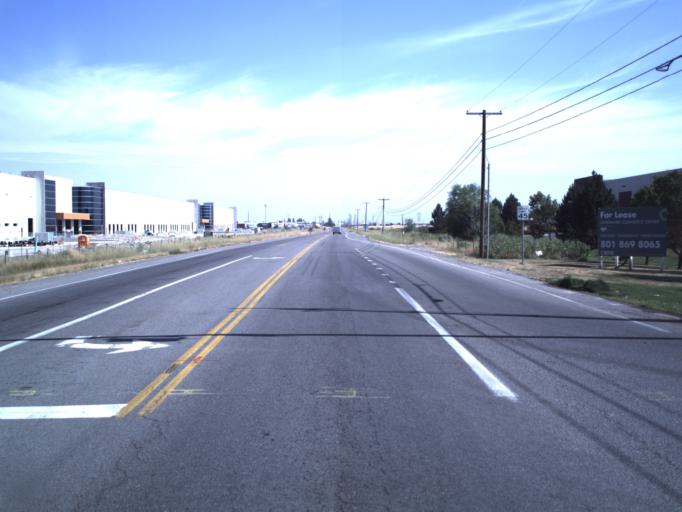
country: US
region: Utah
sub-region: Salt Lake County
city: West Valley City
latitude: 40.7325
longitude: -112.0249
